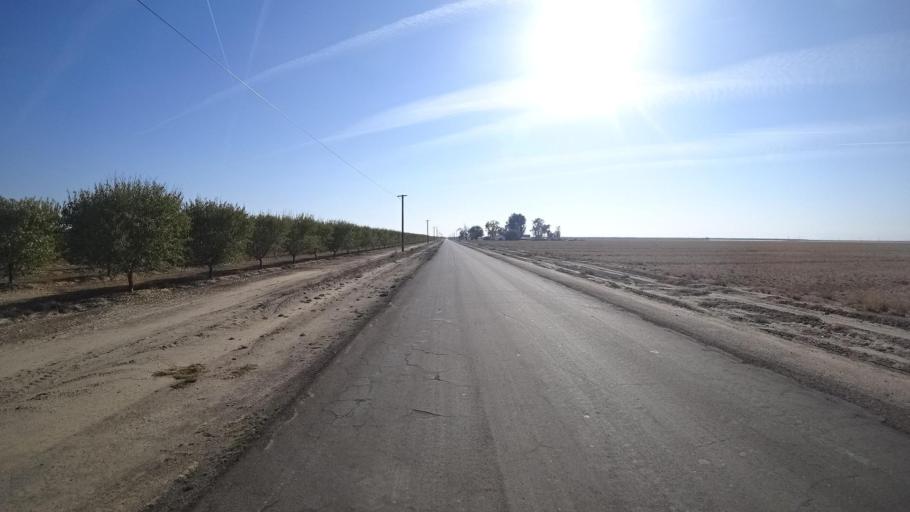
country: US
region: California
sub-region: Kern County
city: Wasco
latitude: 35.6705
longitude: -119.3840
